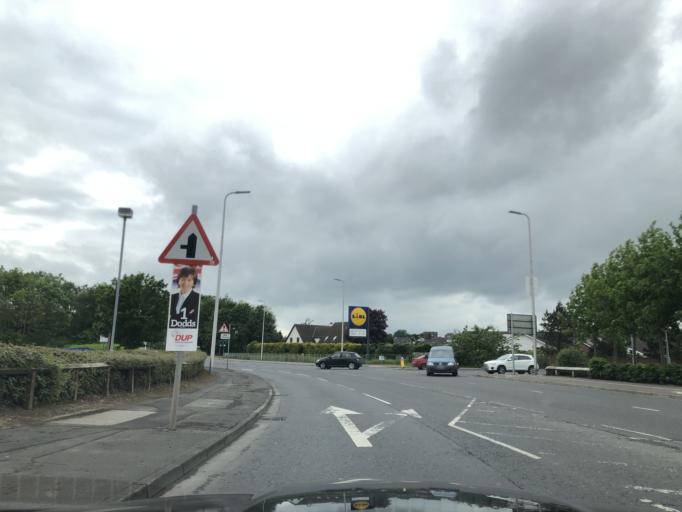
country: GB
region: Northern Ireland
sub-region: Lisburn District
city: Lisburn
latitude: 54.5155
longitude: -6.0558
